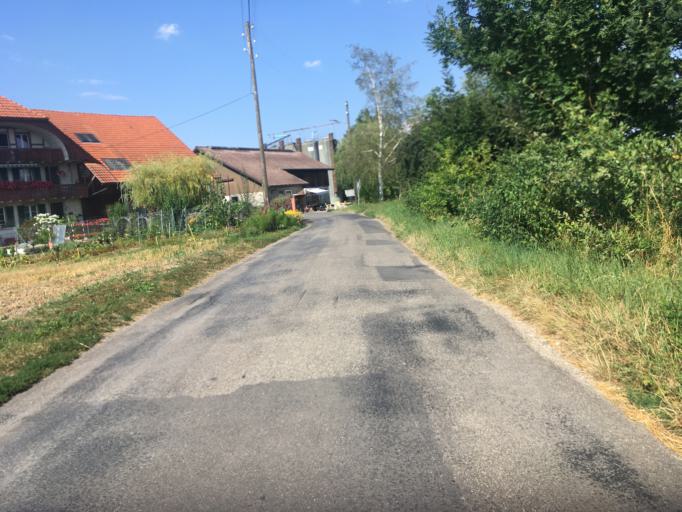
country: CH
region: Bern
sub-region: Biel/Bienne District
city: Lengnau
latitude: 47.1591
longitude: 7.3898
